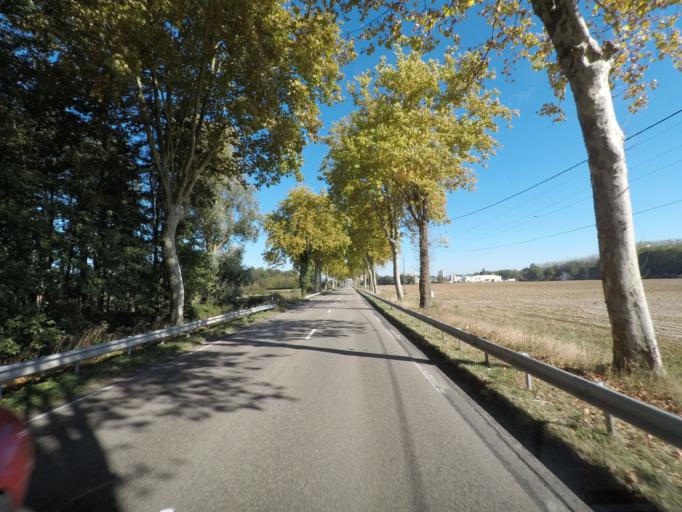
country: FR
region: Rhone-Alpes
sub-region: Departement de l'Ain
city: Servas
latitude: 46.1218
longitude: 5.1567
